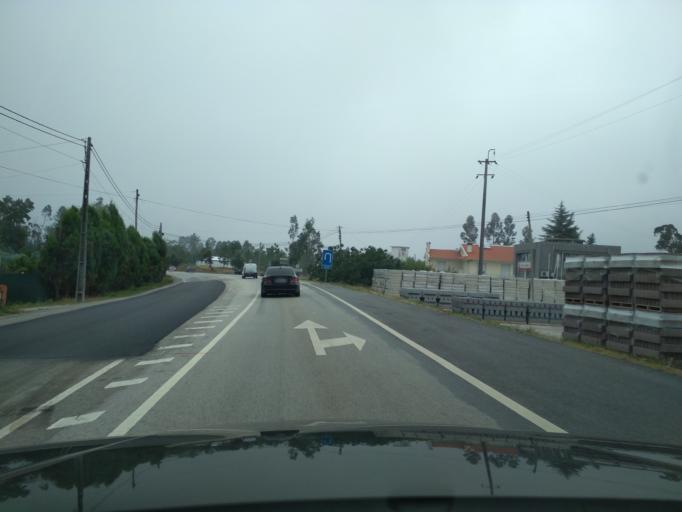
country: PT
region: Aveiro
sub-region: Mealhada
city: Pampilhosa do Botao
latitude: 40.3352
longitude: -8.4507
